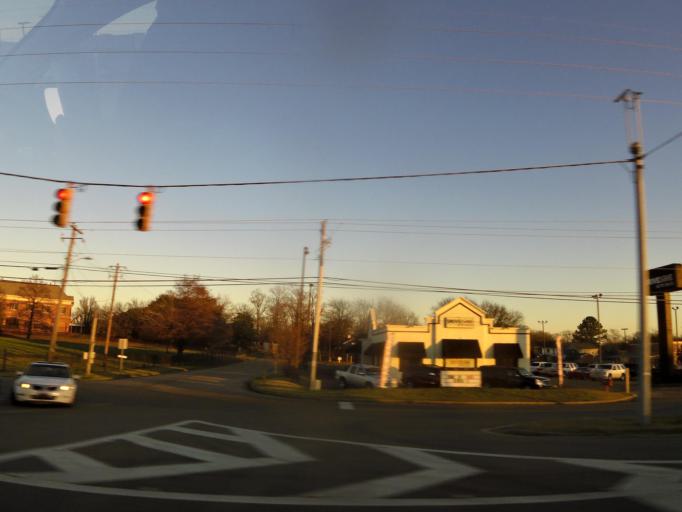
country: US
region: Alabama
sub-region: Montgomery County
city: Montgomery
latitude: 32.3410
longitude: -86.2256
